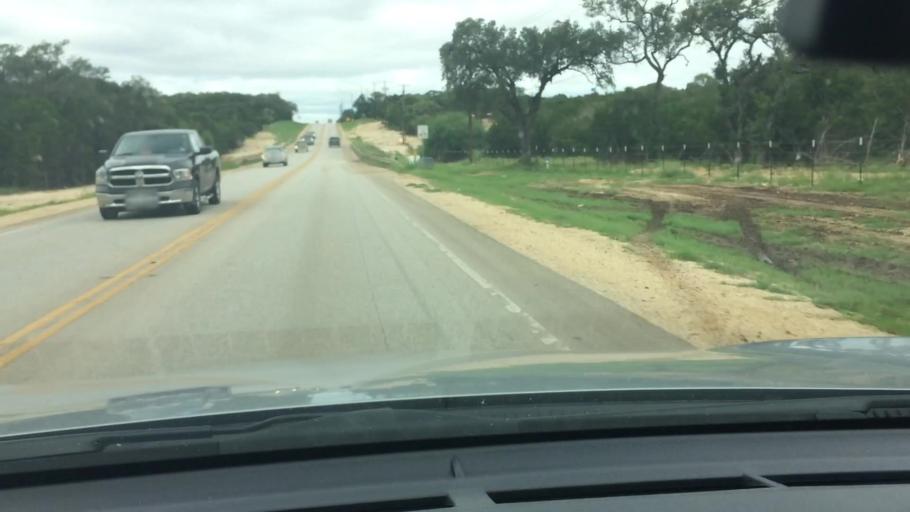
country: US
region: Texas
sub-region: Comal County
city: Garden Ridge
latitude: 29.6419
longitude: -98.3848
